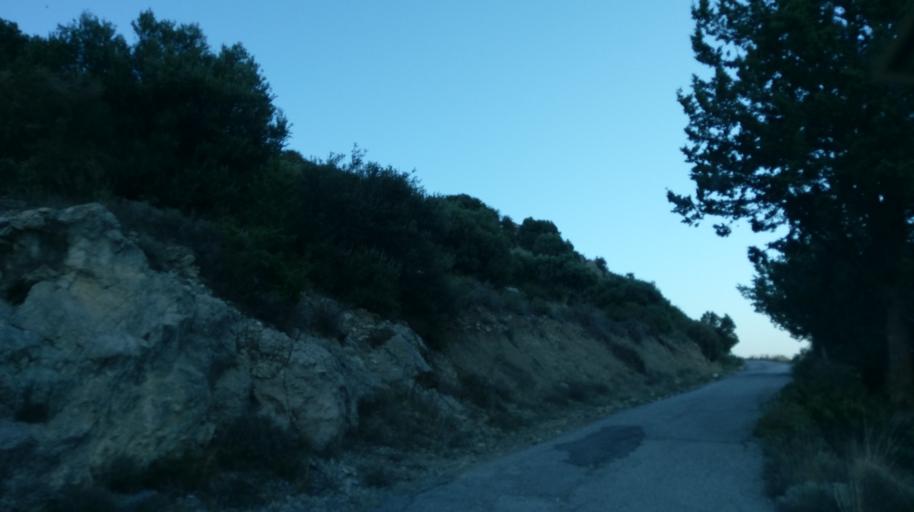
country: CY
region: Ammochostos
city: Trikomo
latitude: 35.3804
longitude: 33.9011
